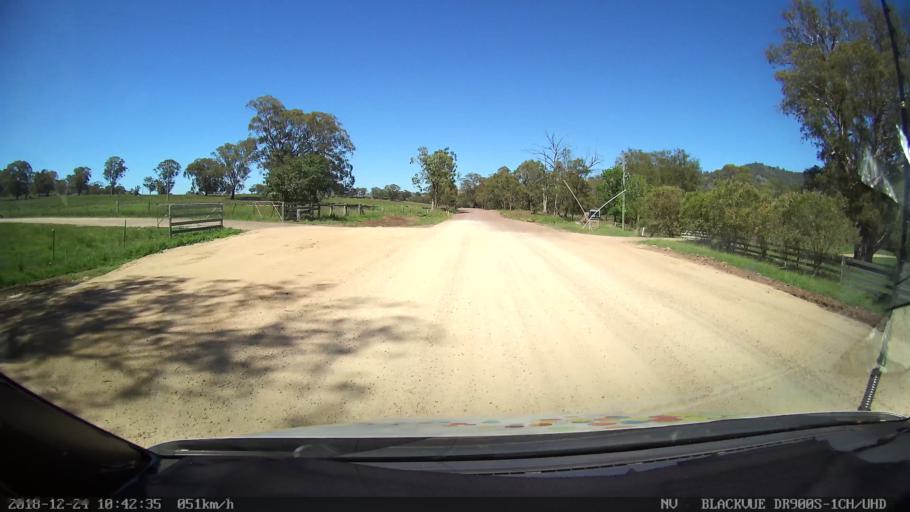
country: AU
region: New South Wales
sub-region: Upper Hunter Shire
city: Merriwa
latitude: -31.8773
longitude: 150.4522
